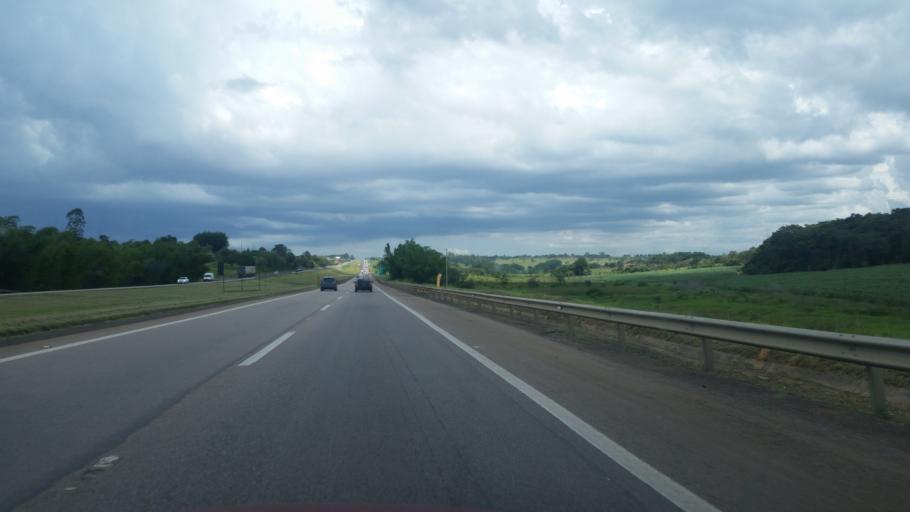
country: BR
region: Sao Paulo
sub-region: Boituva
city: Boituva
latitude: -23.2879
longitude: -47.7597
